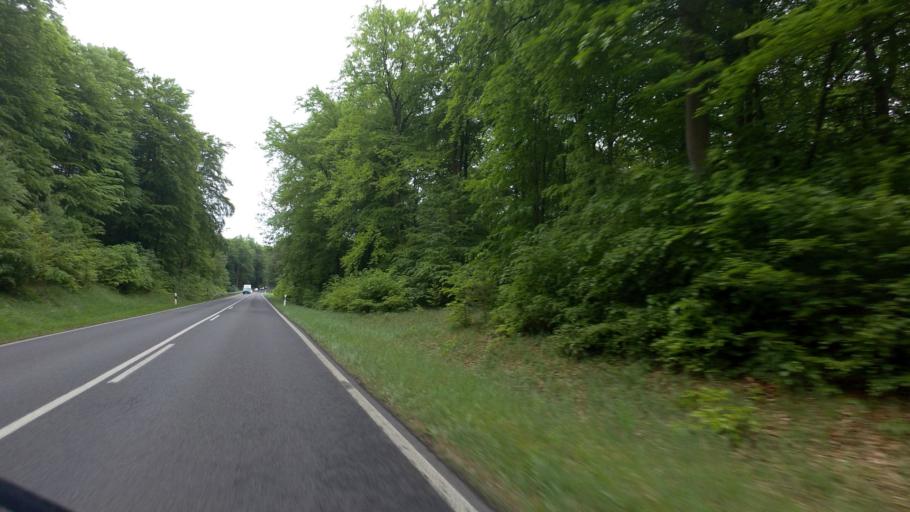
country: DE
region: Brandenburg
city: Lychen
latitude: 53.1842
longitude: 13.3300
